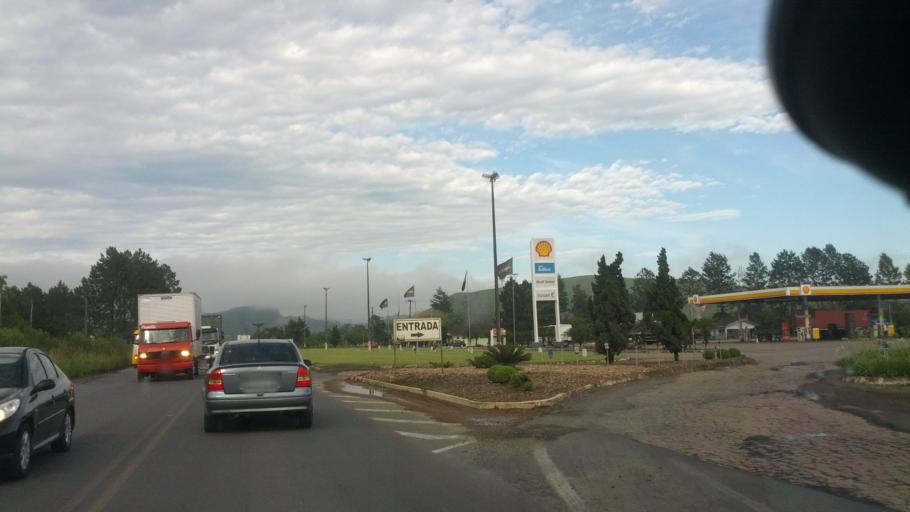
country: BR
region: Santa Catarina
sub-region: Otacilio Costa
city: Otacilio Costa
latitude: -27.2497
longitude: -49.9880
